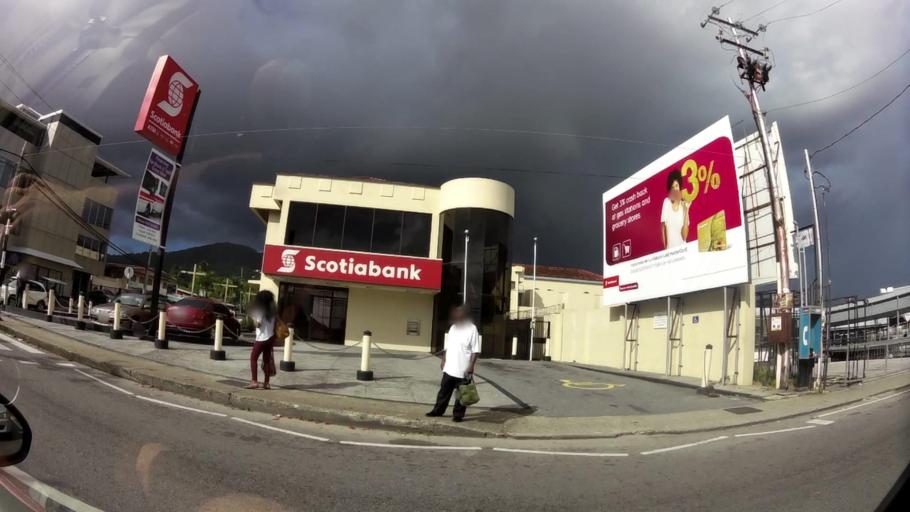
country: TT
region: Tunapuna/Piarco
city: Tunapuna
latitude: 10.6451
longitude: -61.3956
